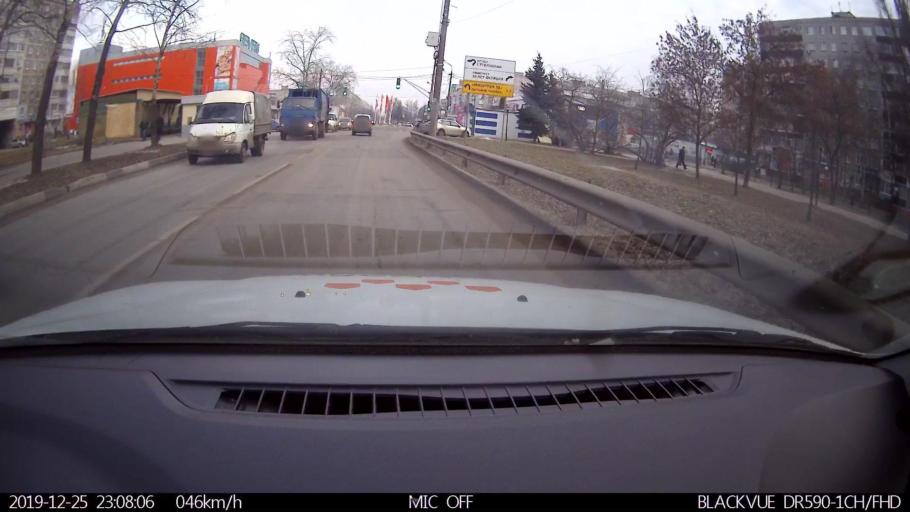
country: RU
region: Nizjnij Novgorod
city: Gorbatovka
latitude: 56.3633
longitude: 43.8139
